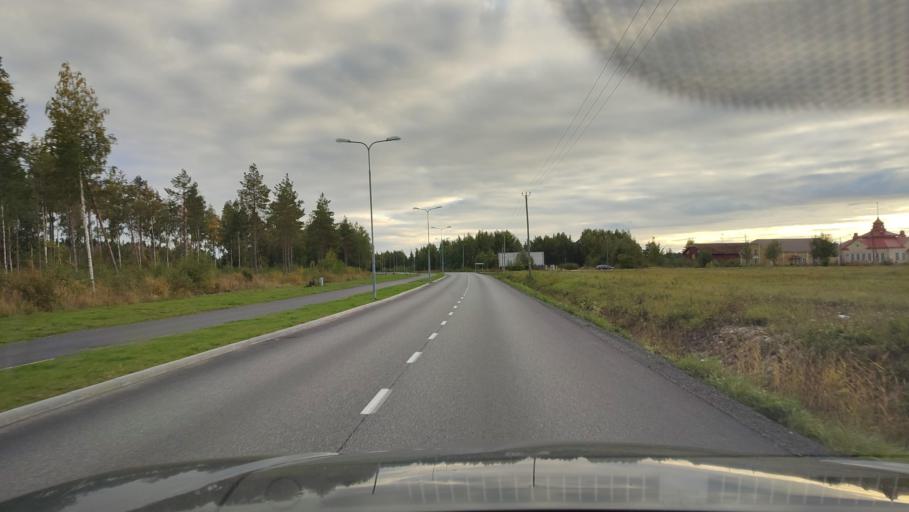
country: FI
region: Ostrobothnia
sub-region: Sydosterbotten
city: Kristinestad
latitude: 62.2660
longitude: 21.3848
